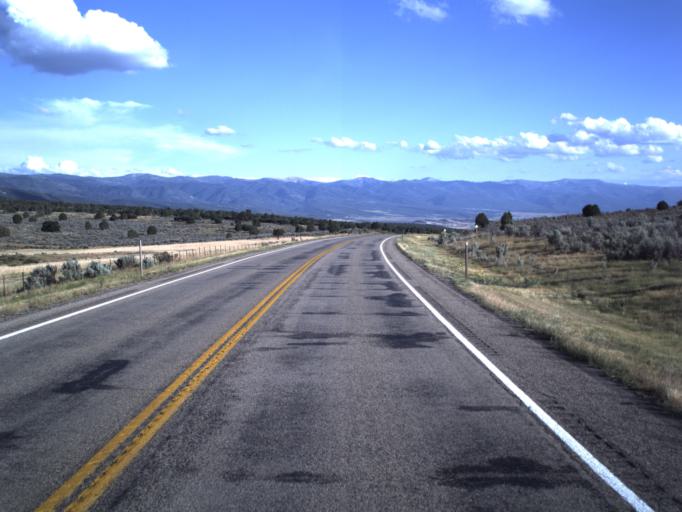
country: US
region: Utah
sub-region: Sanpete County
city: Fairview
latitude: 39.6924
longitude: -111.4608
